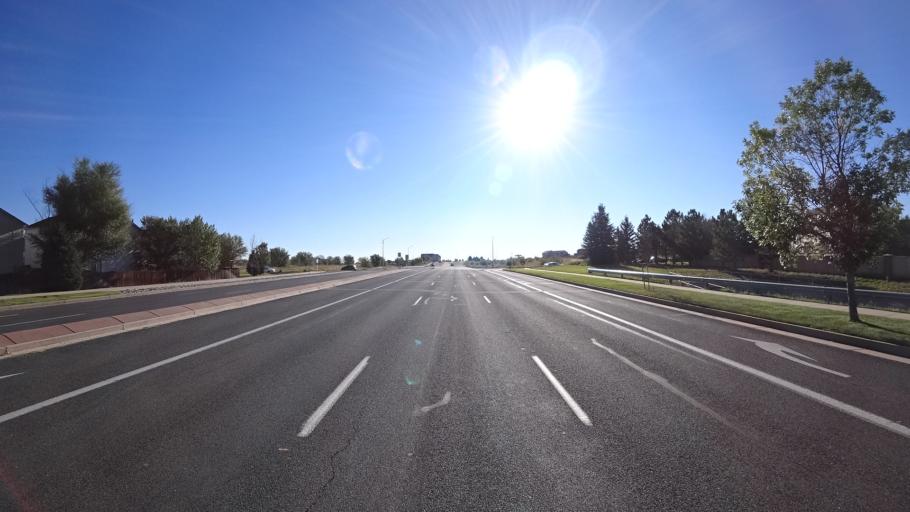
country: US
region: Colorado
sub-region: El Paso County
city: Security-Widefield
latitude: 38.7888
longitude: -104.7346
